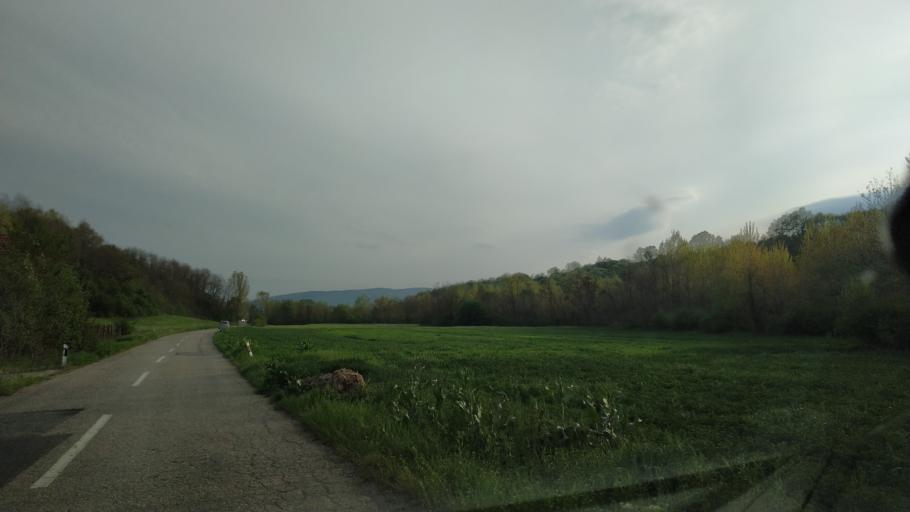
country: RS
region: Central Serbia
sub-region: Nisavski Okrug
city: Aleksinac
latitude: 43.4609
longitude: 21.8027
